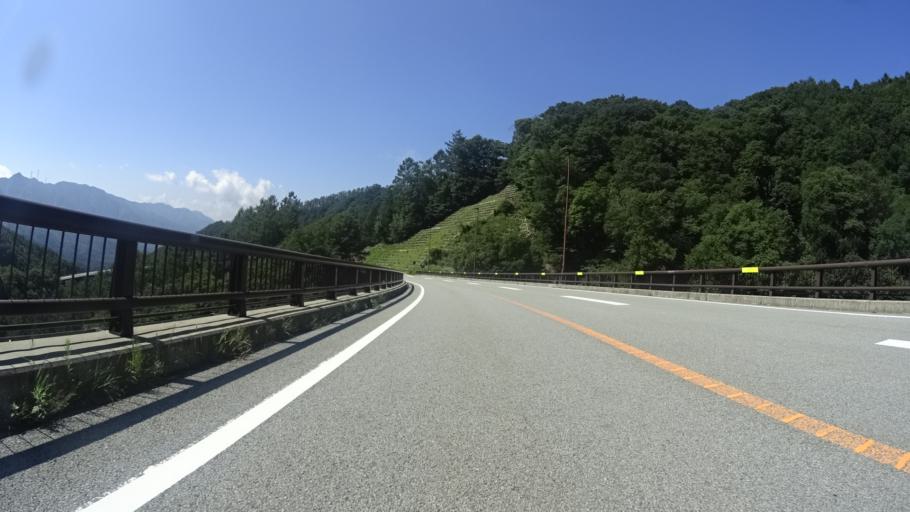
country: JP
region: Yamanashi
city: Enzan
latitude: 35.7609
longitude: 138.8064
